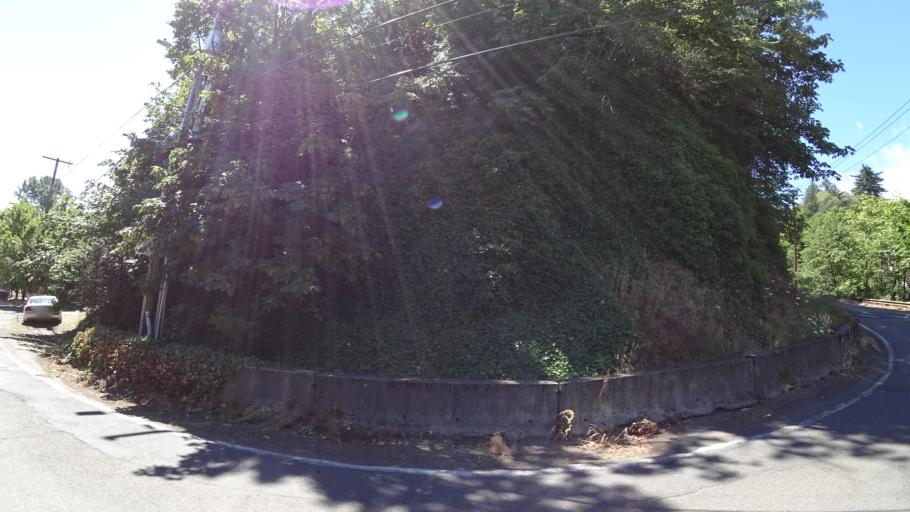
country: US
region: Oregon
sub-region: Multnomah County
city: Portland
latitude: 45.5147
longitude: -122.6935
